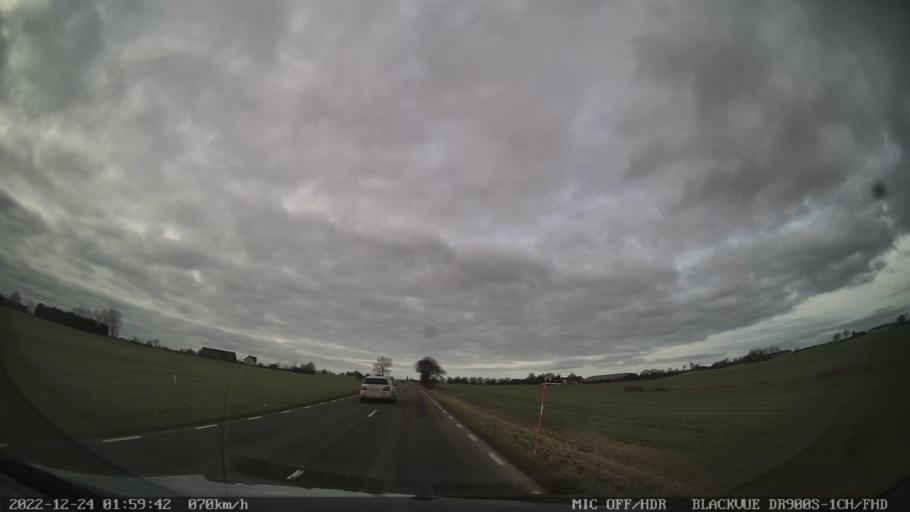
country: SE
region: Skane
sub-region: Tomelilla Kommun
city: Tomelilla
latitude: 55.6094
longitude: 14.0111
